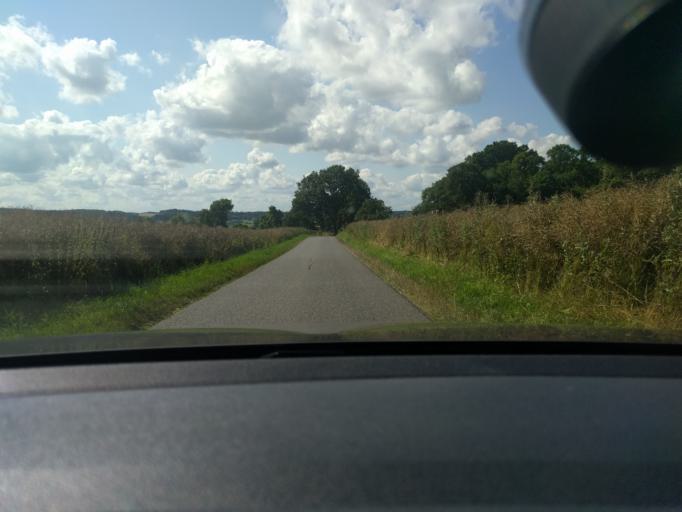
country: DK
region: Central Jutland
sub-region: Viborg Kommune
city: Bjerringbro
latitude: 56.4609
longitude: 9.5920
